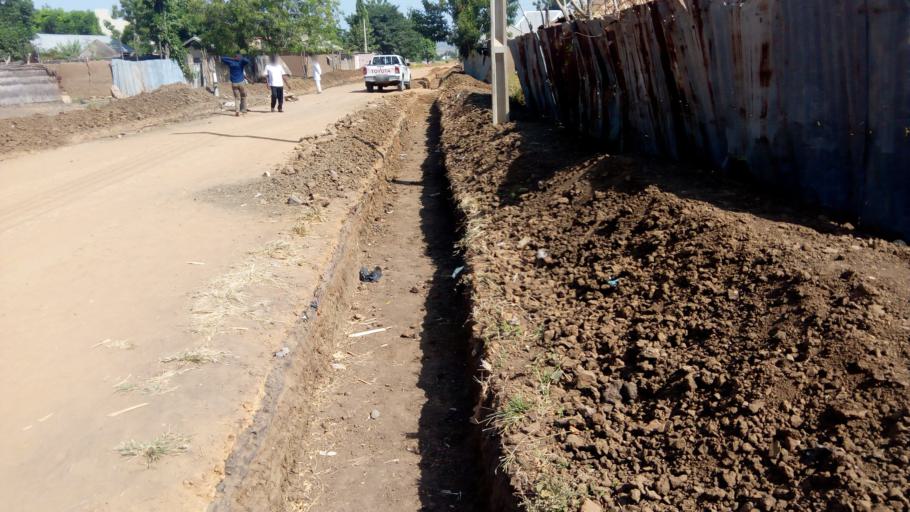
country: NG
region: Adamawa
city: Numan
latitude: 9.6469
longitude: 11.8347
